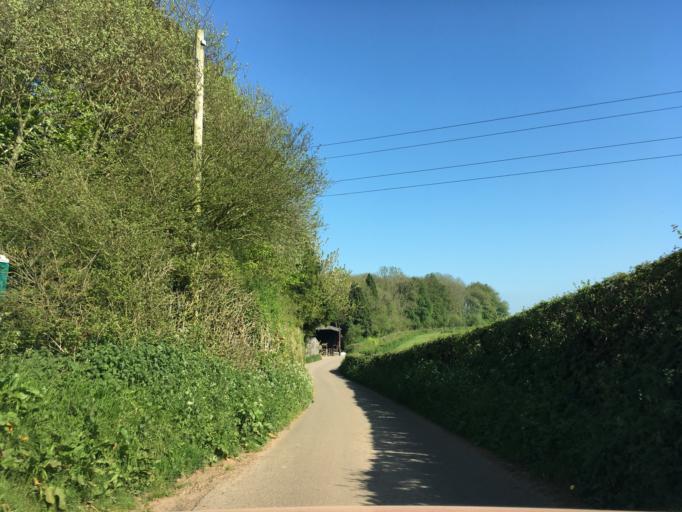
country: GB
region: Wales
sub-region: Monmouthshire
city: Chepstow
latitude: 51.6390
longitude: -2.7220
